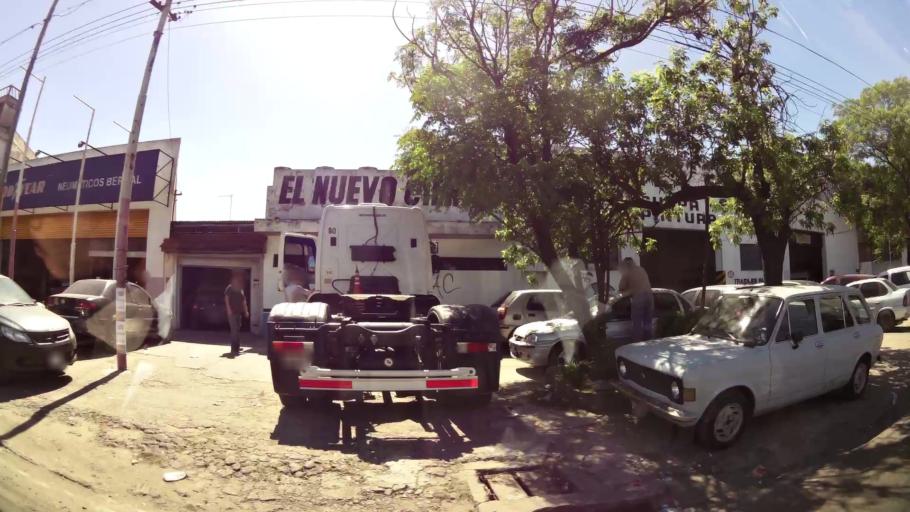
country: AR
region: Buenos Aires
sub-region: Partido de Quilmes
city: Quilmes
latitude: -34.7238
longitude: -58.3026
